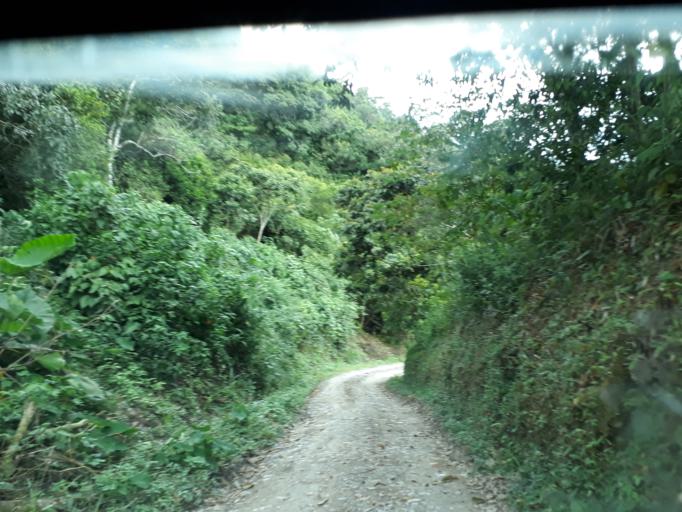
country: CO
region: Cundinamarca
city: Topaipi
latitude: 5.2729
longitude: -74.3546
